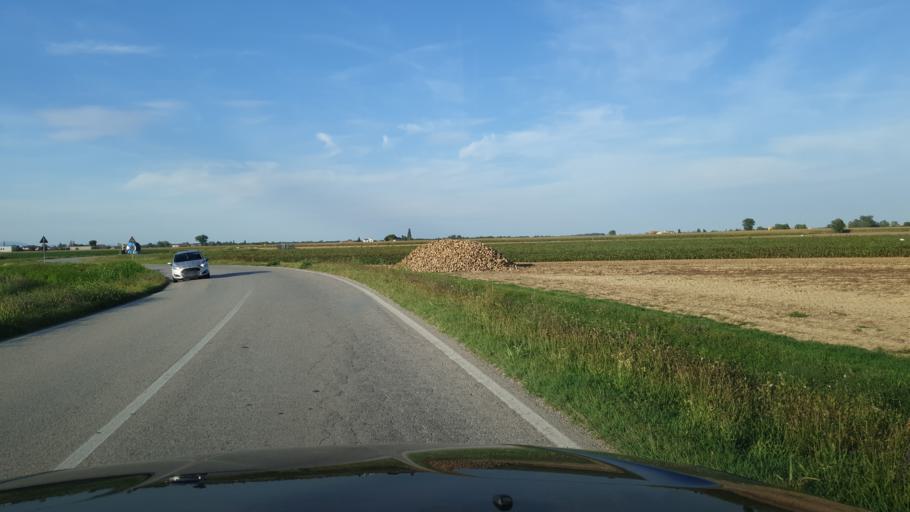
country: IT
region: Veneto
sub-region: Provincia di Rovigo
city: Fiesso Umbertiano
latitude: 44.9758
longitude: 11.6080
